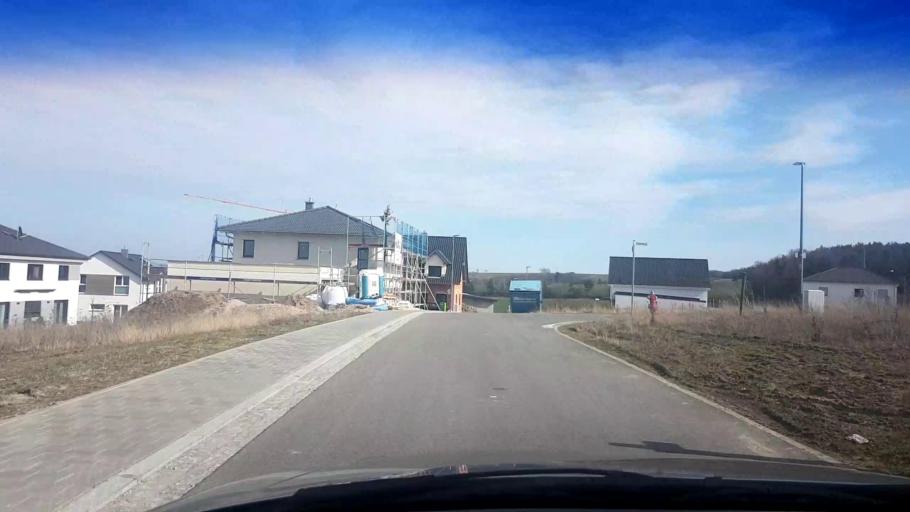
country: DE
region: Bavaria
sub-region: Upper Franconia
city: Burgebrach
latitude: 49.8194
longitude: 10.7397
